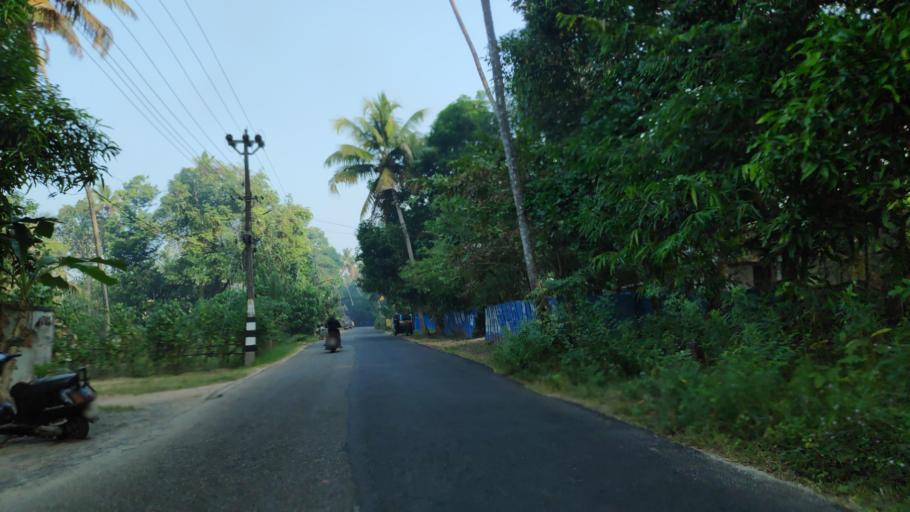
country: IN
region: Kerala
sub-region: Alappuzha
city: Vayalar
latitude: 9.6972
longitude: 76.2901
